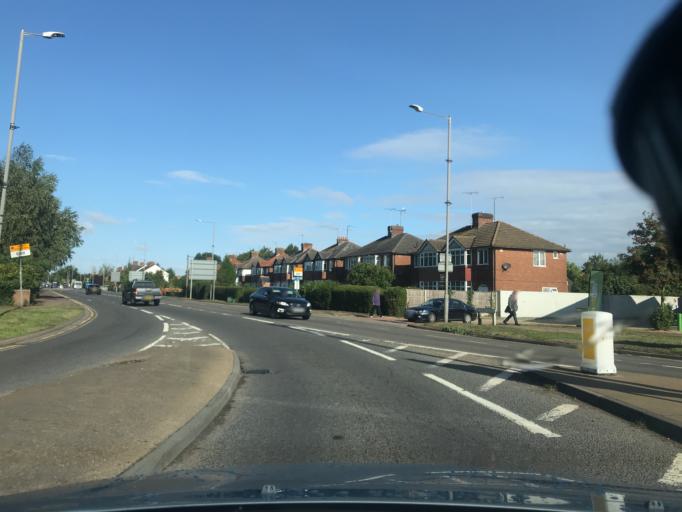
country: GB
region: England
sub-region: Buckinghamshire
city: Aylesbury
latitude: 51.8229
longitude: -0.8257
